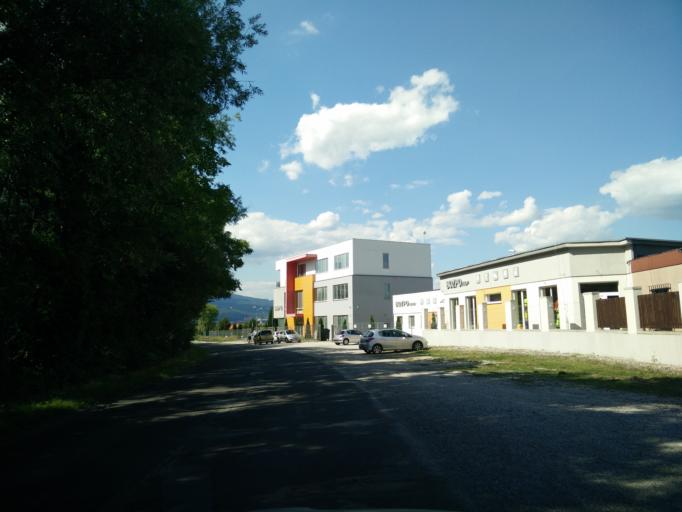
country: SK
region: Nitriansky
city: Prievidza
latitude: 48.7542
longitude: 18.6227
